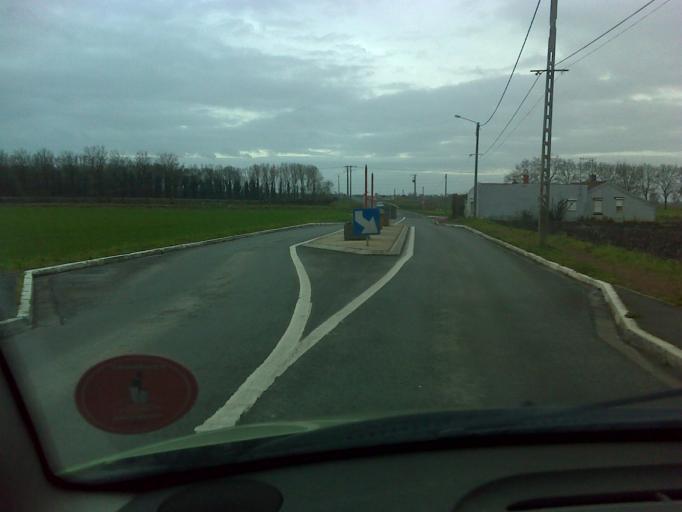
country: FR
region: Nord-Pas-de-Calais
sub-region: Departement du Nord
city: Houplin-Ancoisne
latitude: 50.5603
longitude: 3.0006
